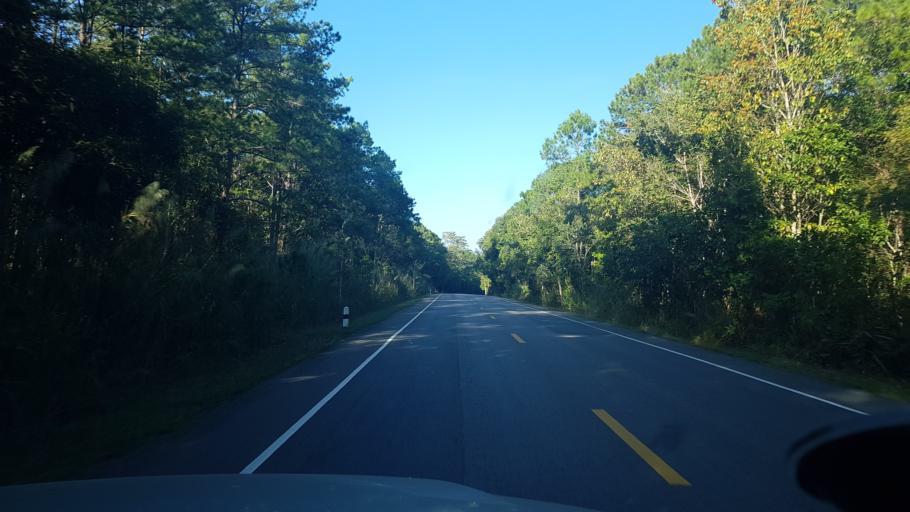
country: TH
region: Phetchabun
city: Nam Nao
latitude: 16.7258
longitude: 101.5750
